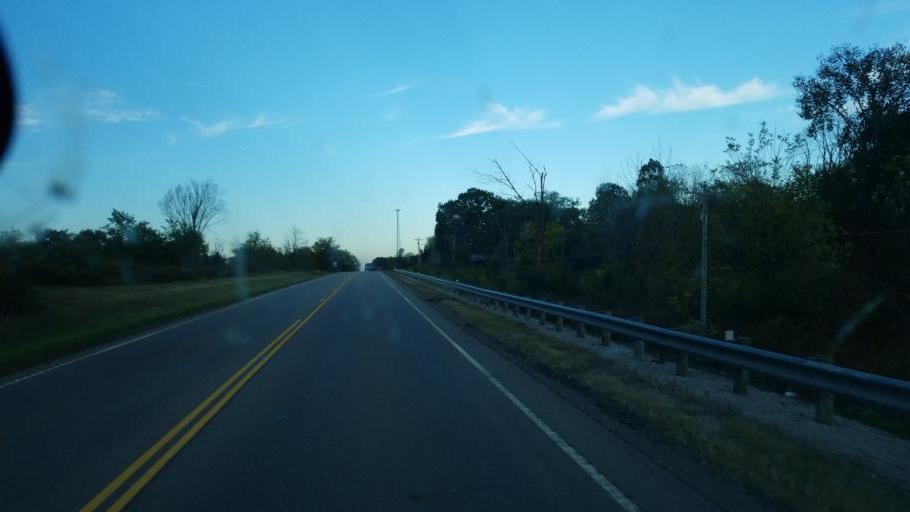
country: US
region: Ohio
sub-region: Licking County
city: Johnstown
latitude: 40.1982
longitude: -82.5887
